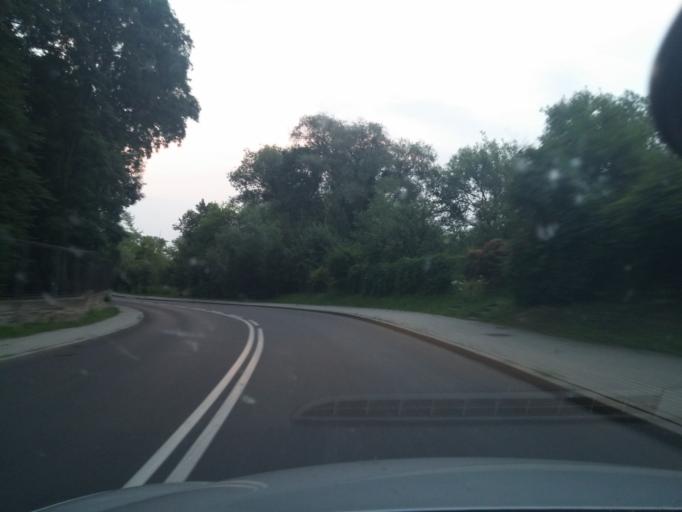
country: PL
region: Subcarpathian Voivodeship
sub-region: Przemysl
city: Przemysl
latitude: 49.7726
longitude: 22.7933
